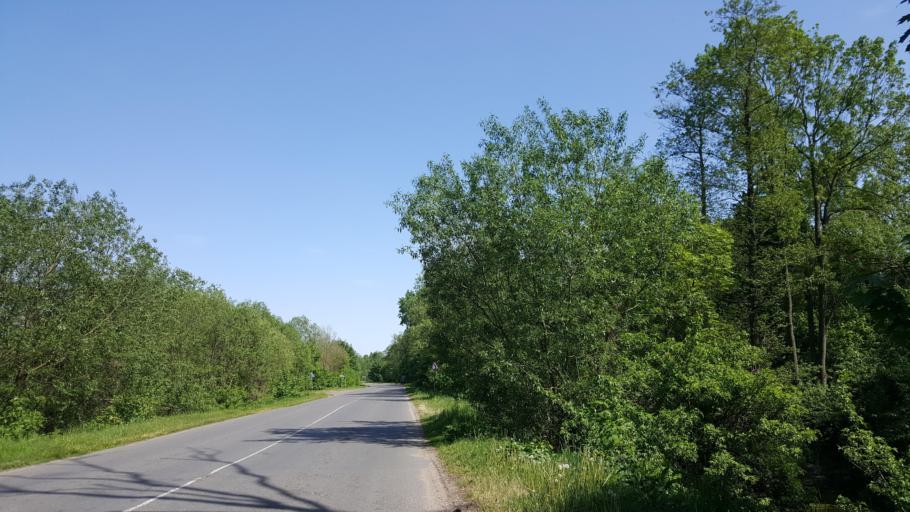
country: BY
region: Brest
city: Charnawchytsy
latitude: 52.2035
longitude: 23.6913
